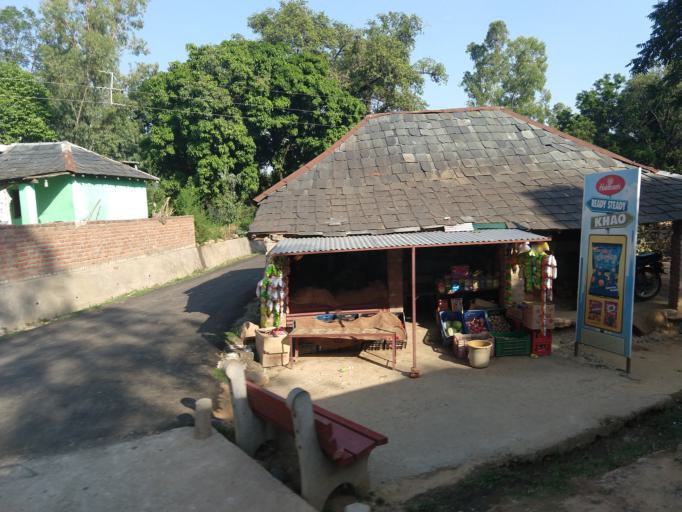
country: IN
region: Himachal Pradesh
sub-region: Chamba
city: Chowari
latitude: 32.3651
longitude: 75.9217
